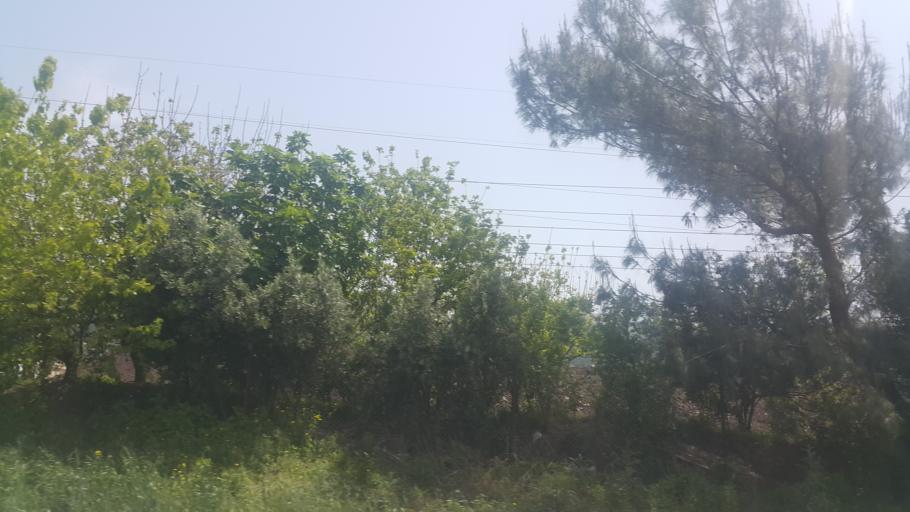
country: TR
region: Hatay
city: Yakacik
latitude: 36.7104
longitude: 36.2191
